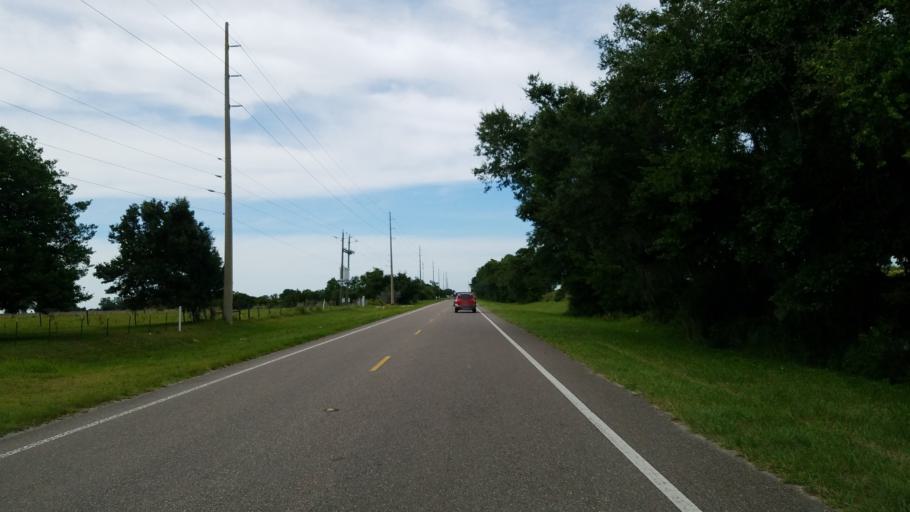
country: US
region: Florida
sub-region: Hillsborough County
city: Balm
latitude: 27.6965
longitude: -82.1461
